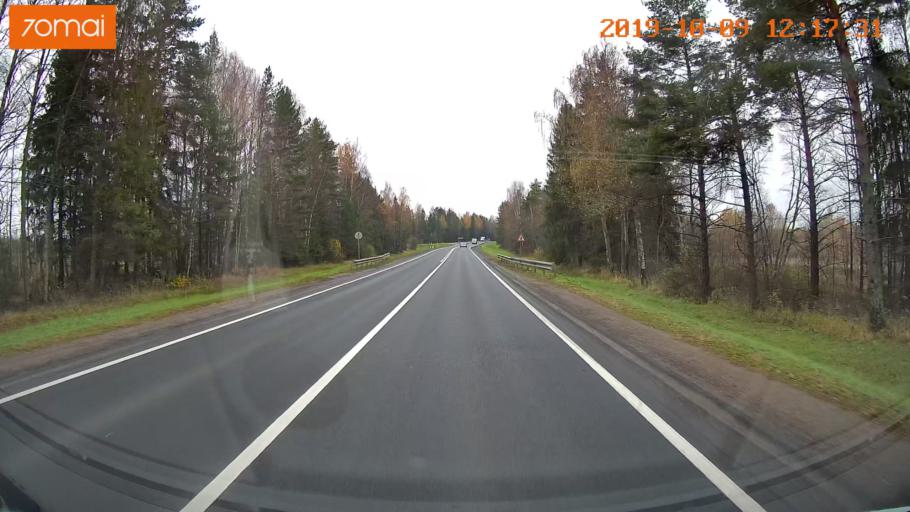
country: RU
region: Jaroslavl
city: Prechistoye
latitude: 58.4551
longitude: 40.3215
